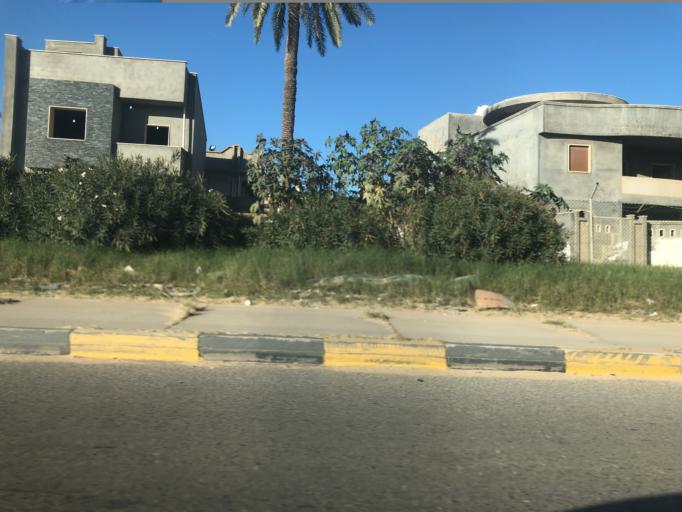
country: LY
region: Tripoli
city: Tagiura
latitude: 32.8700
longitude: 13.2695
